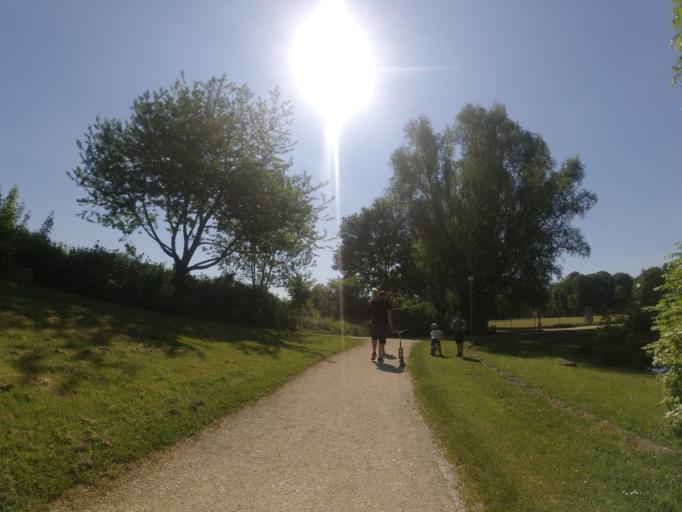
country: DE
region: Bavaria
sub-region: Swabia
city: Neu-Ulm
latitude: 48.4109
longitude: 10.0141
